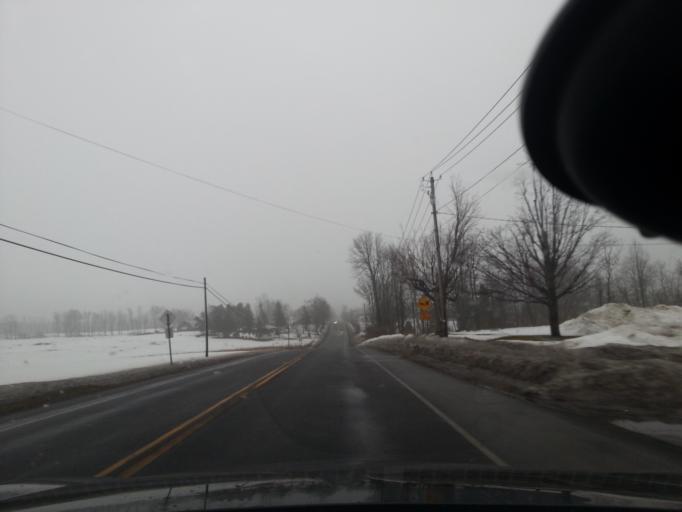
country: US
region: New York
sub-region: St. Lawrence County
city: Ogdensburg
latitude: 44.6126
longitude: -75.4001
